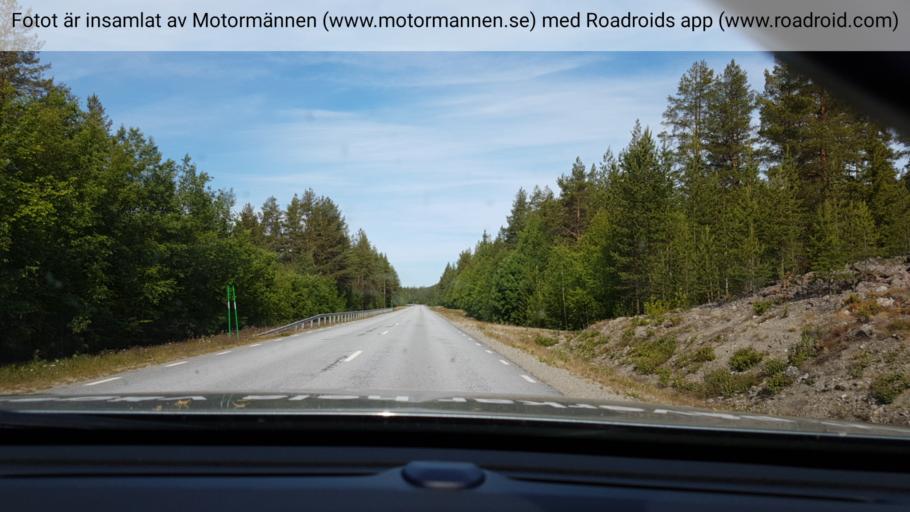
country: SE
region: Vaesterbotten
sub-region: Asele Kommun
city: Asele
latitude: 64.1979
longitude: 17.0680
